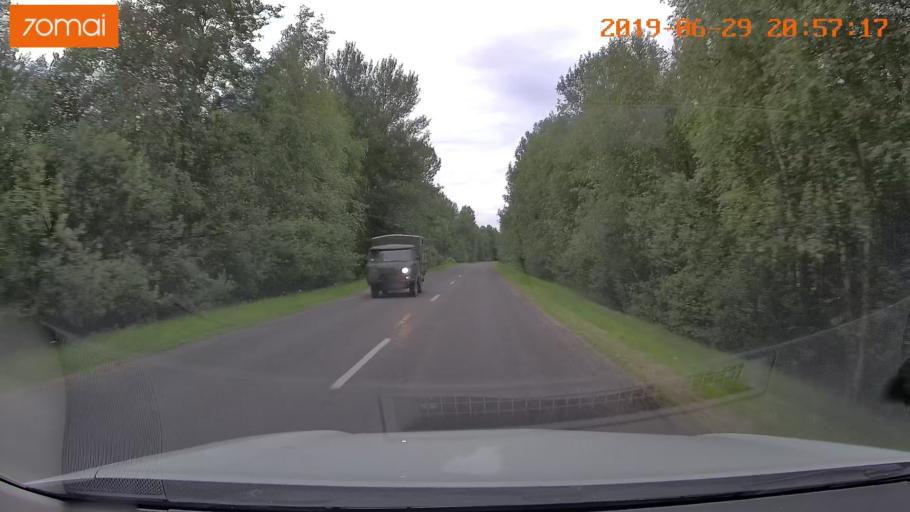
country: BY
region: Brest
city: Hantsavichy
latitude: 52.7169
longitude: 26.3698
